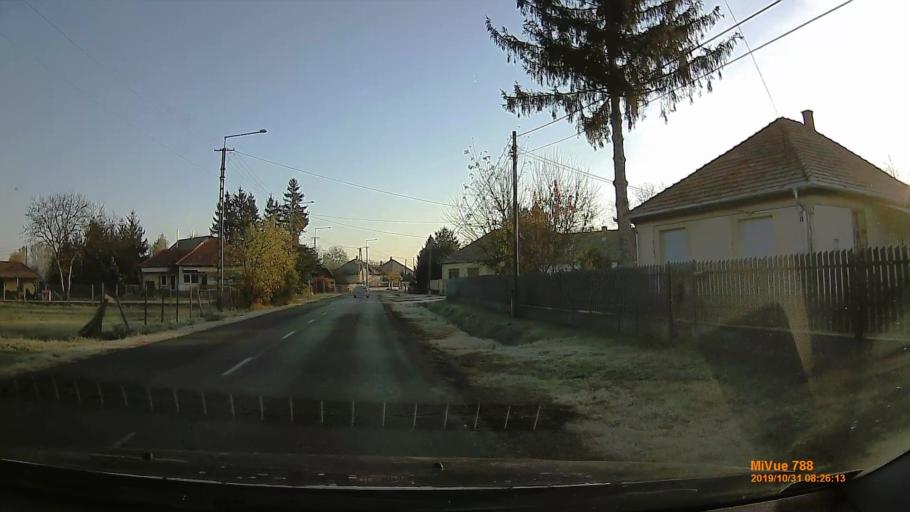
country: HU
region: Pest
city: Tapiobicske
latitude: 47.3648
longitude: 19.6761
